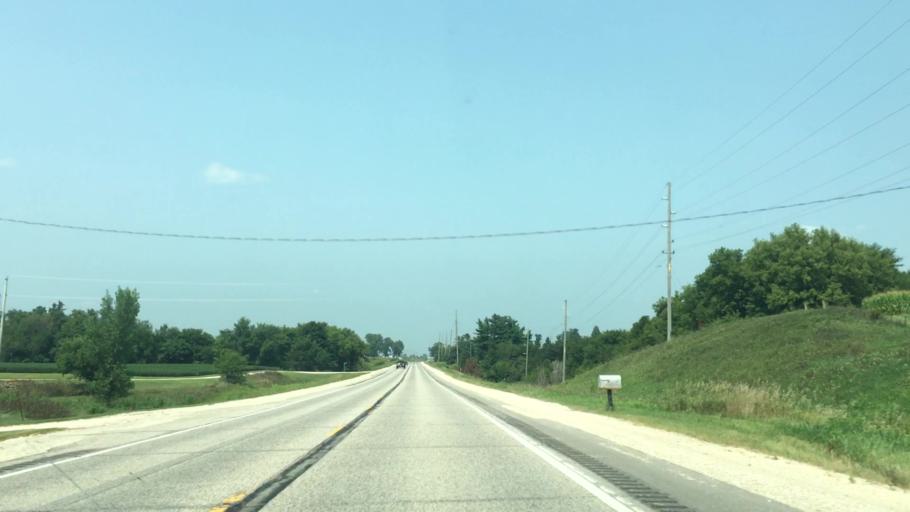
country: US
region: Iowa
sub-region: Fayette County
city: Fayette
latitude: 42.8741
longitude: -91.8104
